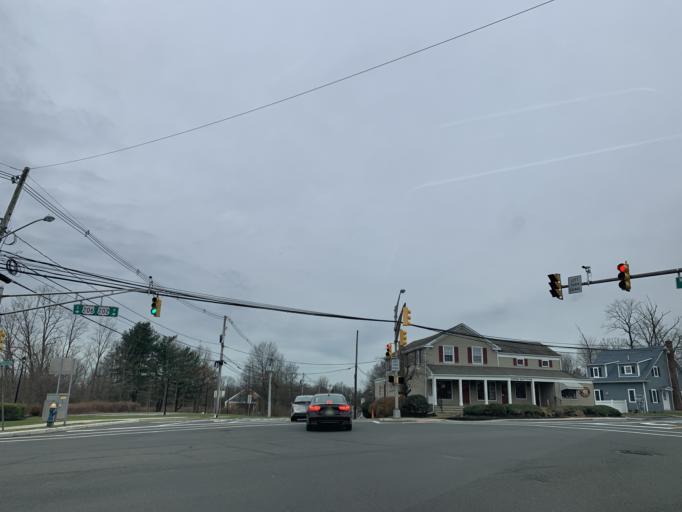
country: US
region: New Jersey
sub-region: Somerset County
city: Bedminster
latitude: 40.6467
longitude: -74.6400
